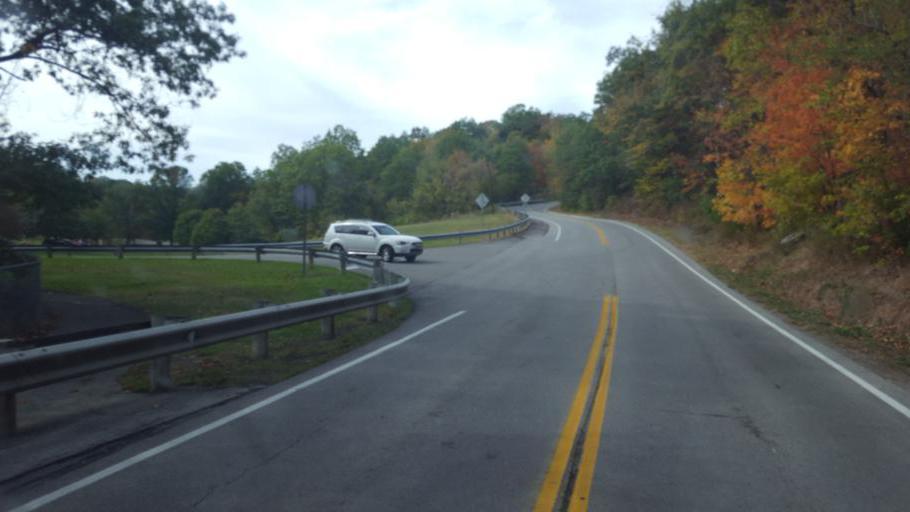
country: US
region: Ohio
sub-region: Lorain County
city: Vermilion-on-the-Lake
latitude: 41.3822
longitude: -82.3169
